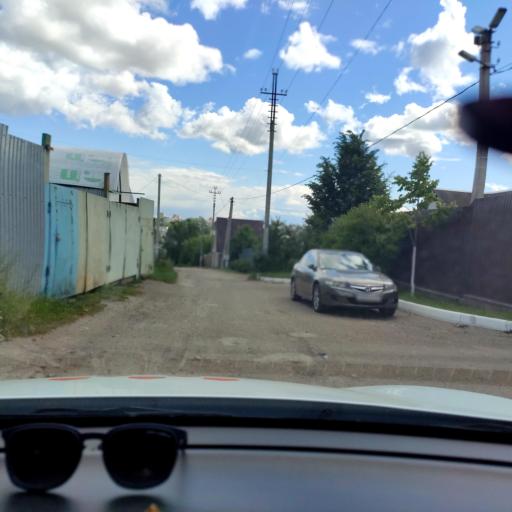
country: RU
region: Tatarstan
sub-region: Gorod Kazan'
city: Kazan
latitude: 55.8846
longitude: 49.0803
